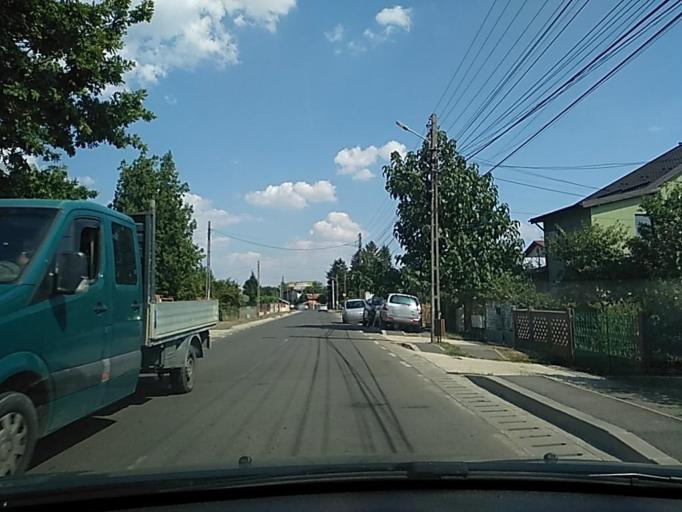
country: RO
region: Ilfov
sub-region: Comuna Domnesti
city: Domnesti
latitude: 44.4049
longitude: 25.9332
